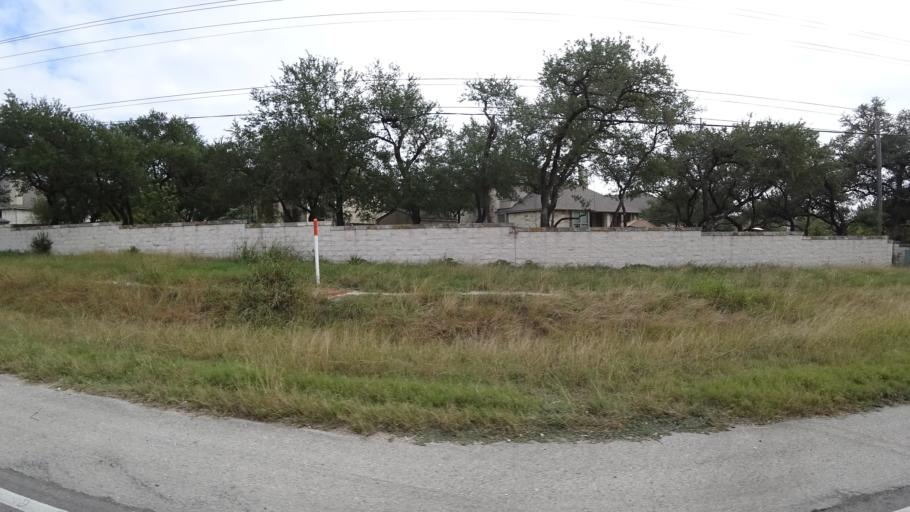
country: US
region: Texas
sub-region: Travis County
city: Shady Hollow
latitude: 30.2011
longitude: -97.9193
